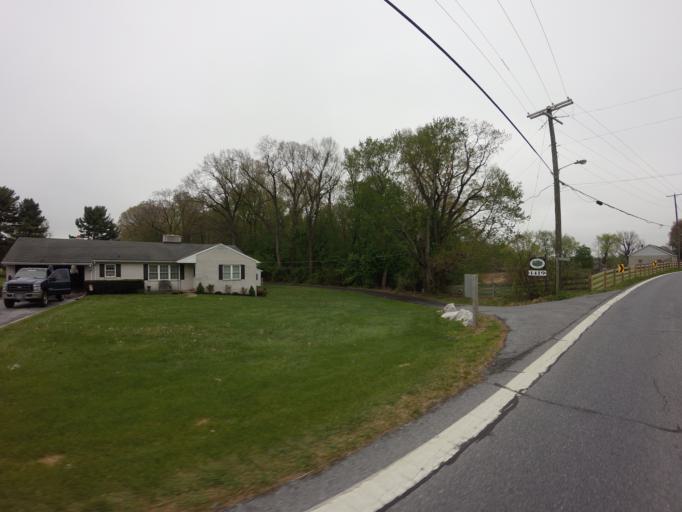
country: US
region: Maryland
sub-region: Baltimore County
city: Hunt Valley
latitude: 39.5891
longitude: -76.6983
